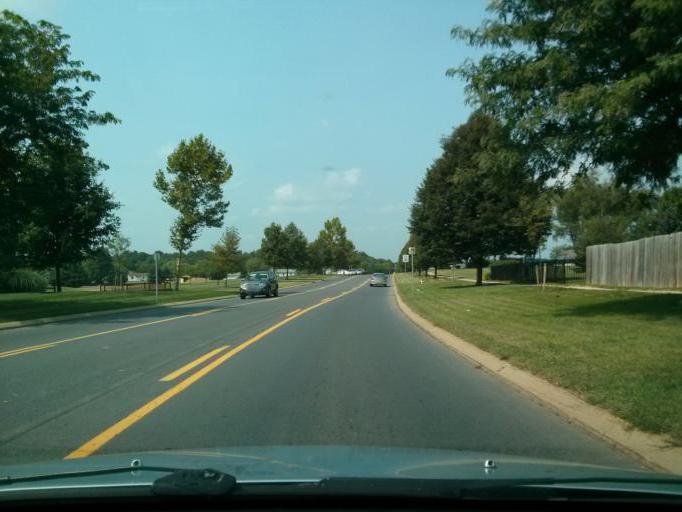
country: US
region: Pennsylvania
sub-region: Centre County
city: State College
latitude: 40.7725
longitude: -77.8721
